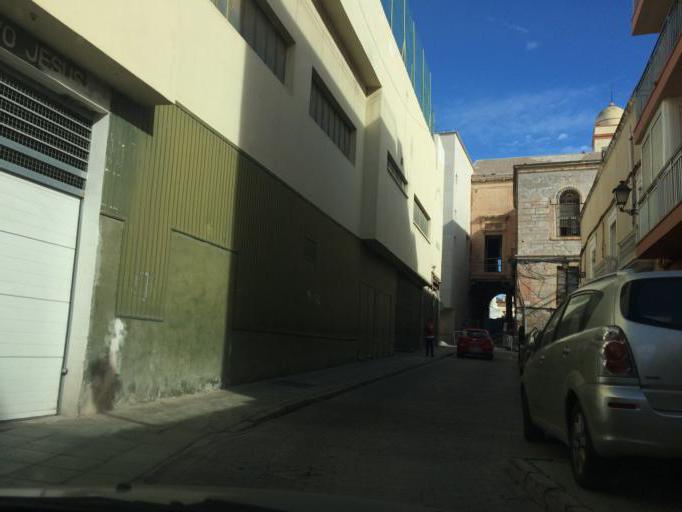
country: ES
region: Andalusia
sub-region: Provincia de Almeria
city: Almeria
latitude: 36.8400
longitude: -2.4686
